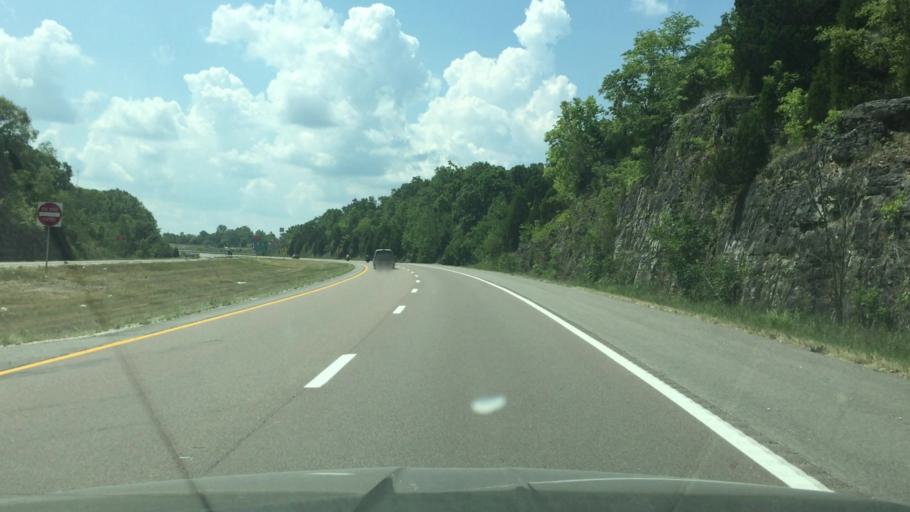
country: US
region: Missouri
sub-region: Miller County
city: Lake Ozark
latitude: 38.2222
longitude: -92.6262
